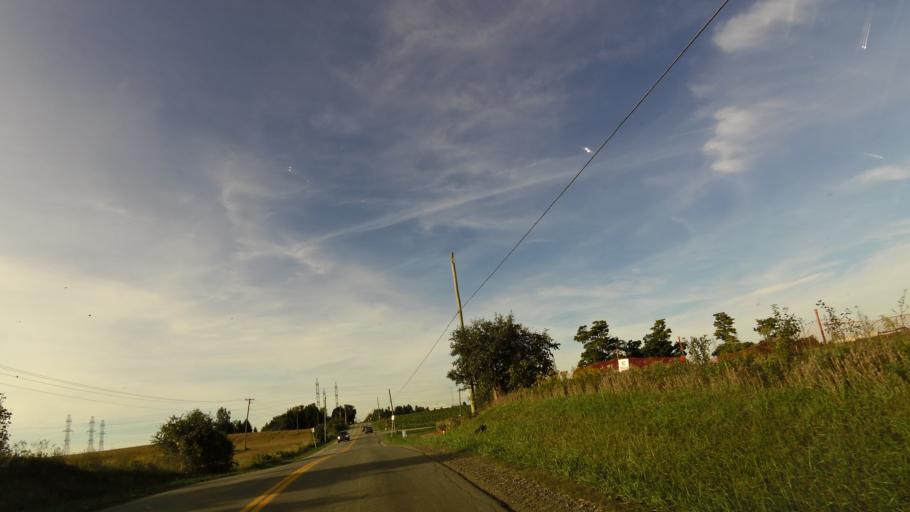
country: CA
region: Ontario
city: Ancaster
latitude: 43.1791
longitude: -80.0374
